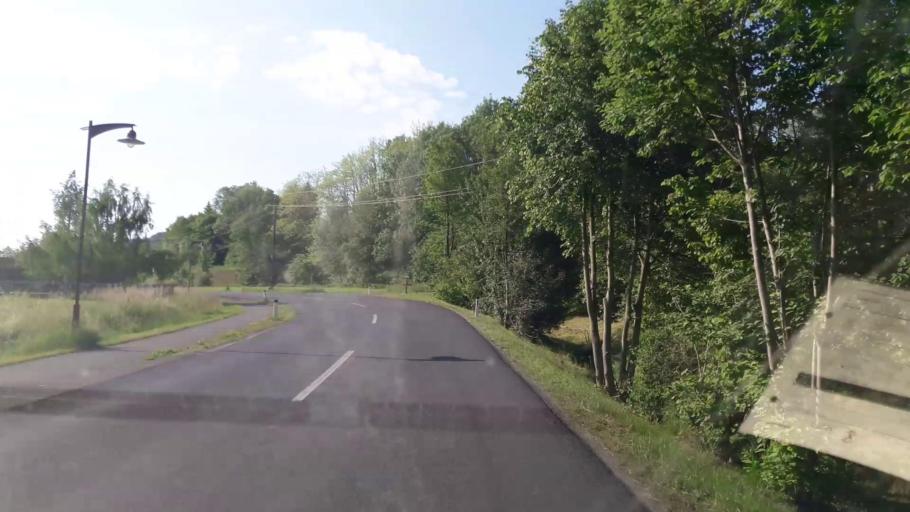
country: AT
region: Styria
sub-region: Politischer Bezirk Suedoststeiermark
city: Unterlamm
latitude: 46.9736
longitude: 16.0628
